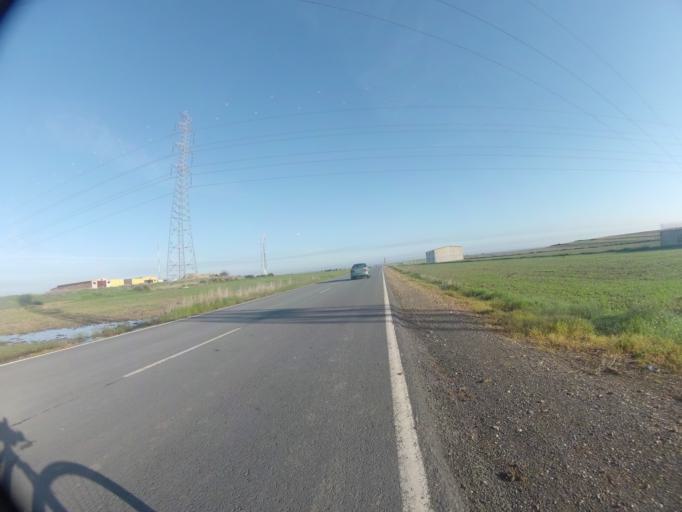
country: ES
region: Andalusia
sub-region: Provincia de Huelva
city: Huelva
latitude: 37.3010
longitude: -6.9259
